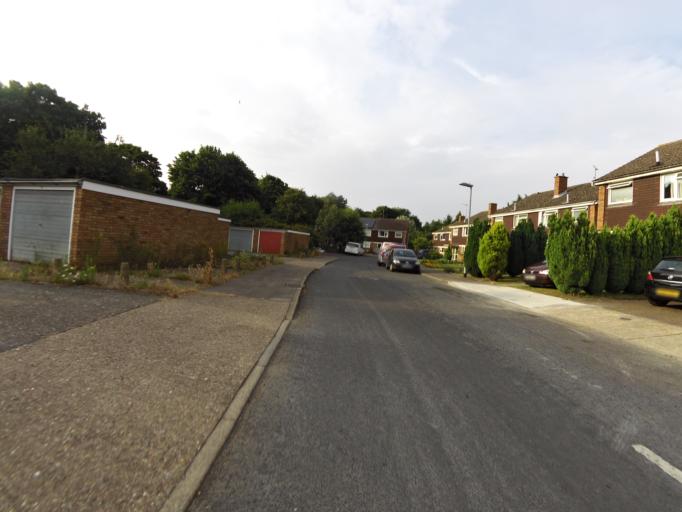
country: GB
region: England
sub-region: Suffolk
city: Ipswich
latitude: 52.0662
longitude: 1.1725
